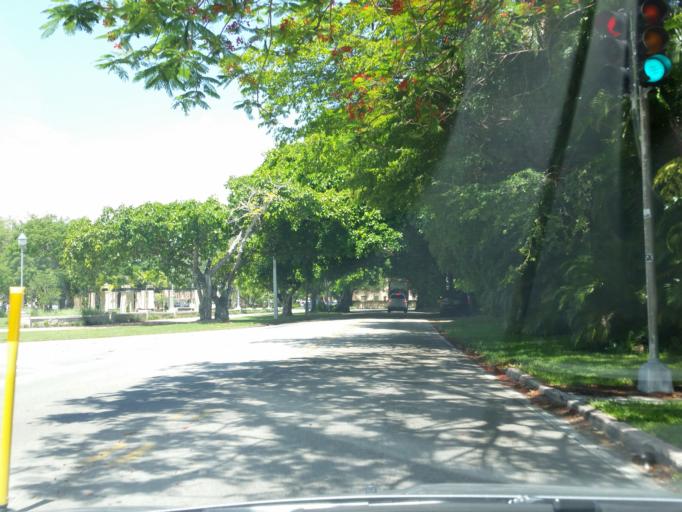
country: US
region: Florida
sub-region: Miami-Dade County
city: Coconut Grove
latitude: 25.7073
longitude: -80.2595
